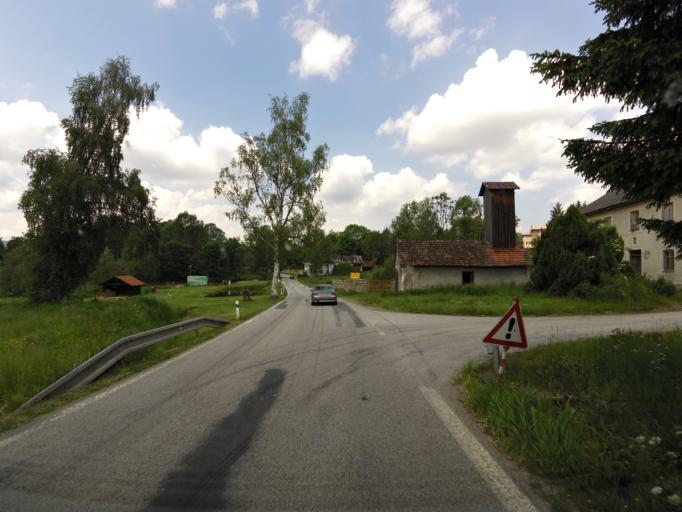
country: CZ
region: Jihocesky
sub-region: Okres Cesky Krumlov
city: Horni Plana
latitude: 48.8100
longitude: 13.9671
